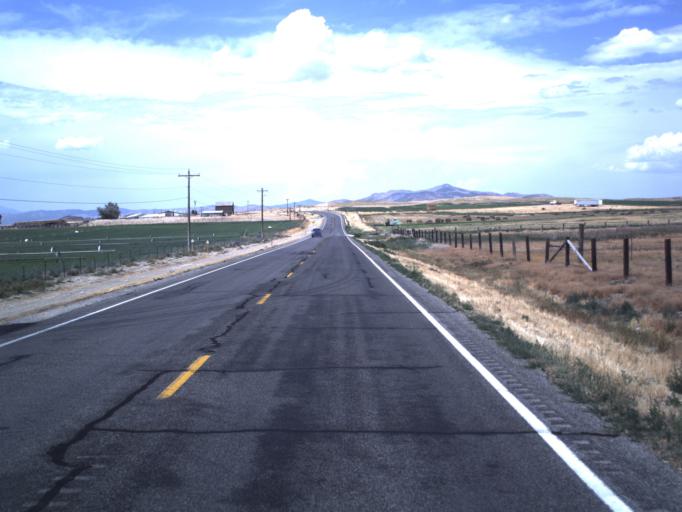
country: US
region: Utah
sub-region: Sanpete County
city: Moroni
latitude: 39.4889
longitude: -111.5631
